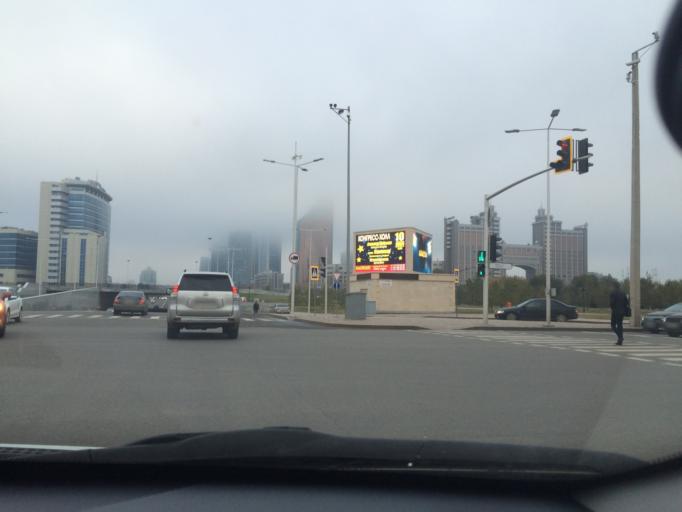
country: KZ
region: Astana Qalasy
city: Astana
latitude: 51.1344
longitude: 71.4073
